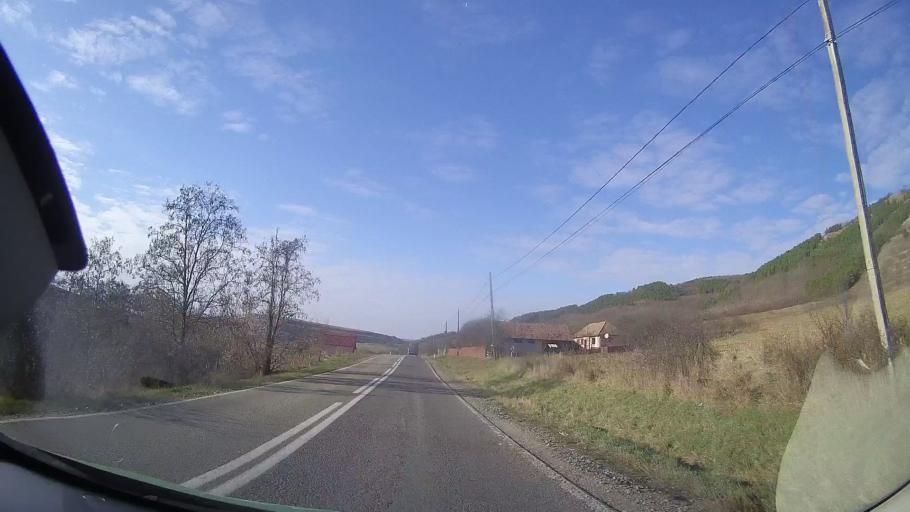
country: RO
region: Cluj
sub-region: Comuna Caianu
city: Caianu
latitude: 46.8000
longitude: 23.9426
